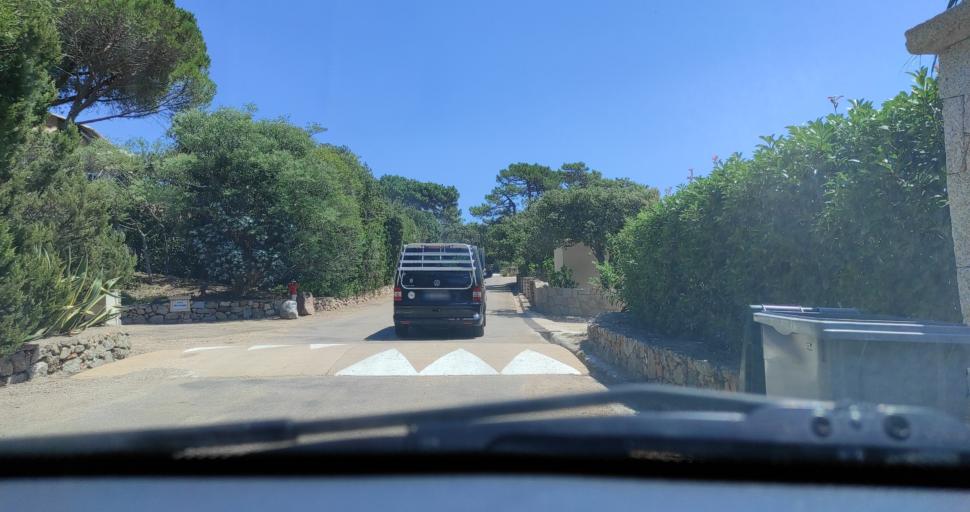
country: FR
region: Corsica
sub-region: Departement de la Corse-du-Sud
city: Porto-Vecchio
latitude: 41.6194
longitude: 9.3521
